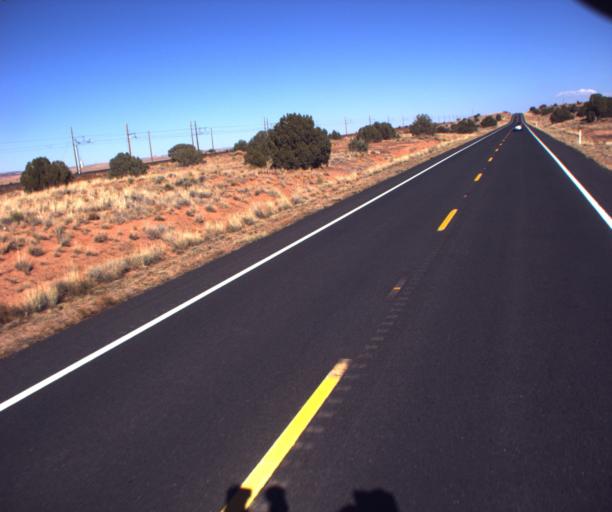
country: US
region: Arizona
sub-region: Coconino County
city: Kaibito
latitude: 36.4064
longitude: -110.8394
